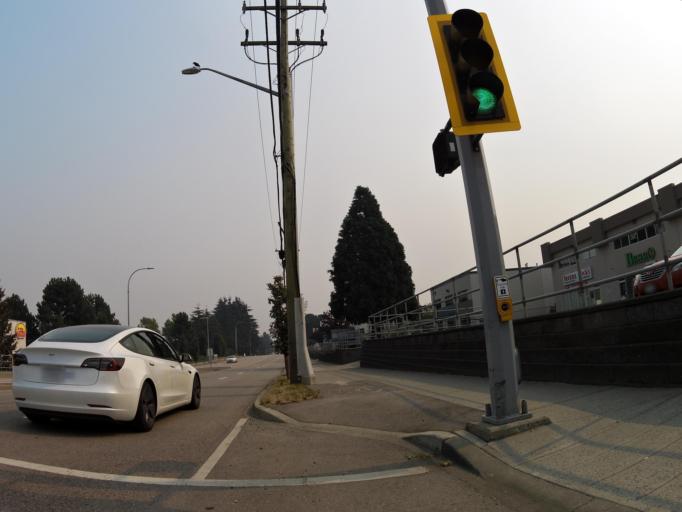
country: CA
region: British Columbia
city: Delta
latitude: 49.1481
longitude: -122.8620
